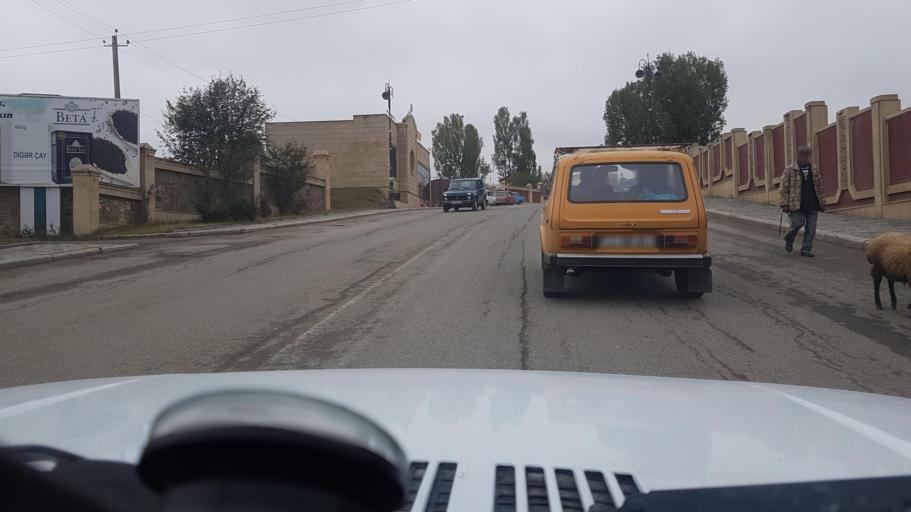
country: AZ
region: Gadabay Rayon
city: Kyadabek
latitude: 40.5812
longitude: 45.8101
